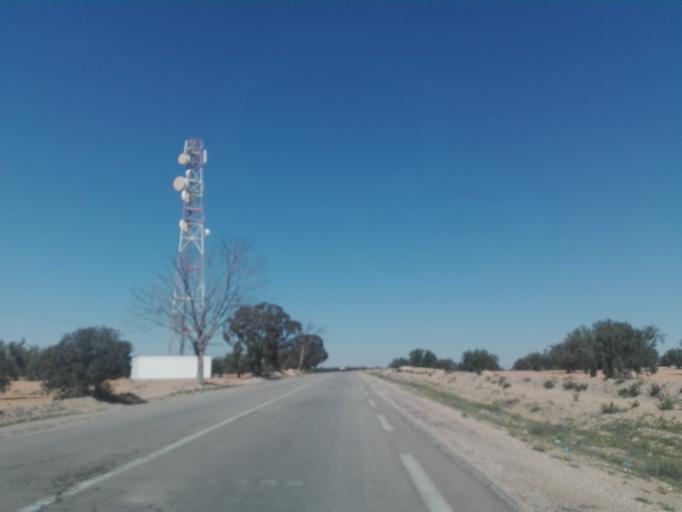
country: TN
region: Safaqis
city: Bi'r `Ali Bin Khalifah
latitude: 34.7558
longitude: 10.3302
